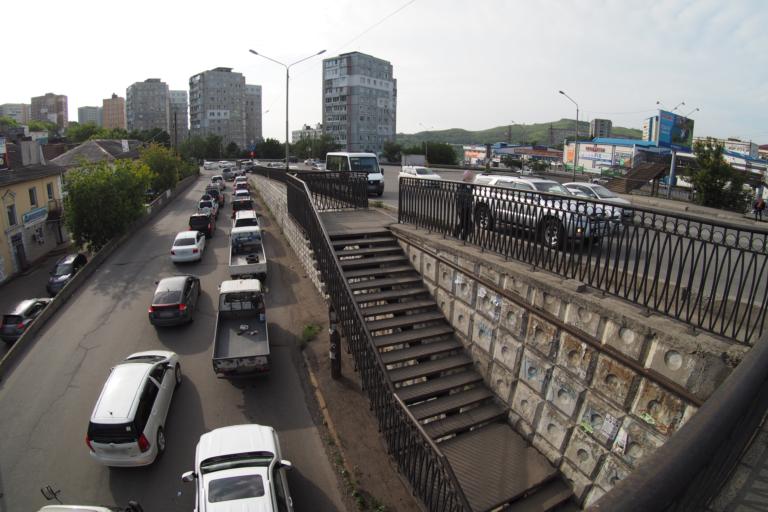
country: RU
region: Primorskiy
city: Vladivostok
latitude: 43.1281
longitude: 131.9396
